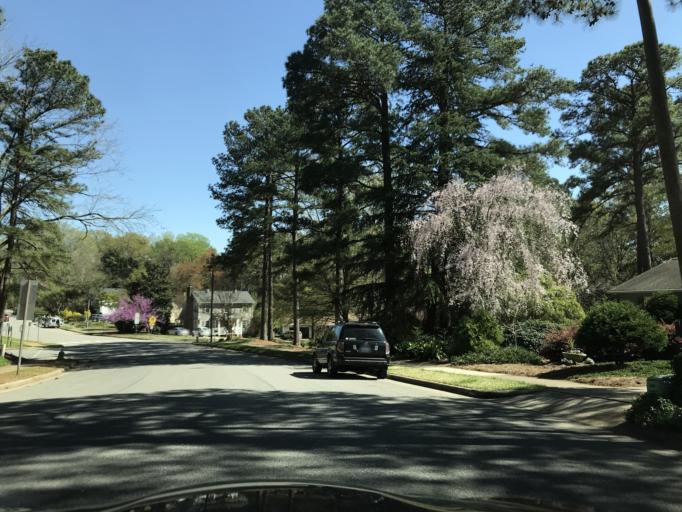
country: US
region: North Carolina
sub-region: Wake County
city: West Raleigh
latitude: 35.7739
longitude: -78.7031
